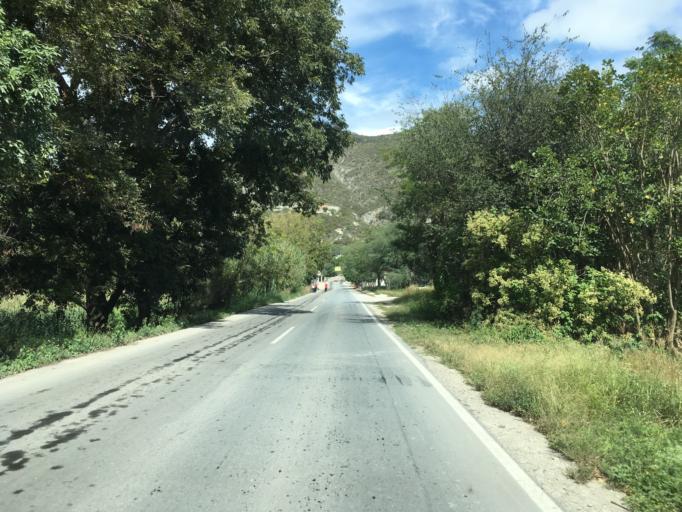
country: MX
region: Hidalgo
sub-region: San Agustin Metzquititlan
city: Mezquititlan
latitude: 20.4974
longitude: -98.6955
